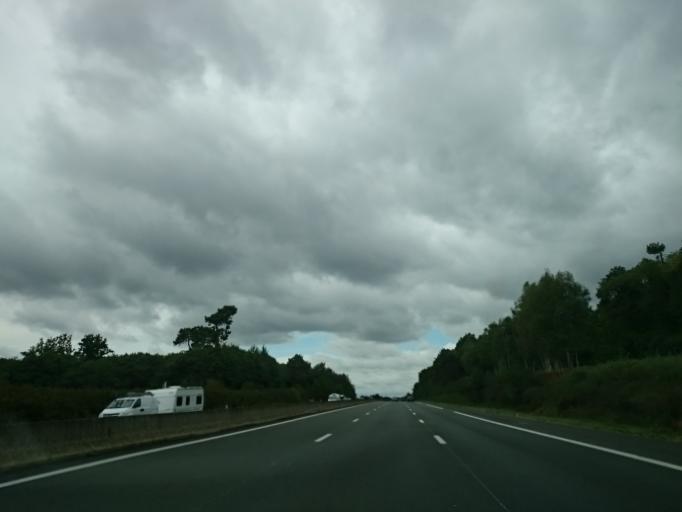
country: FR
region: Pays de la Loire
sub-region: Departement de la Sarthe
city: Tuffe
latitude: 48.0978
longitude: 0.5300
